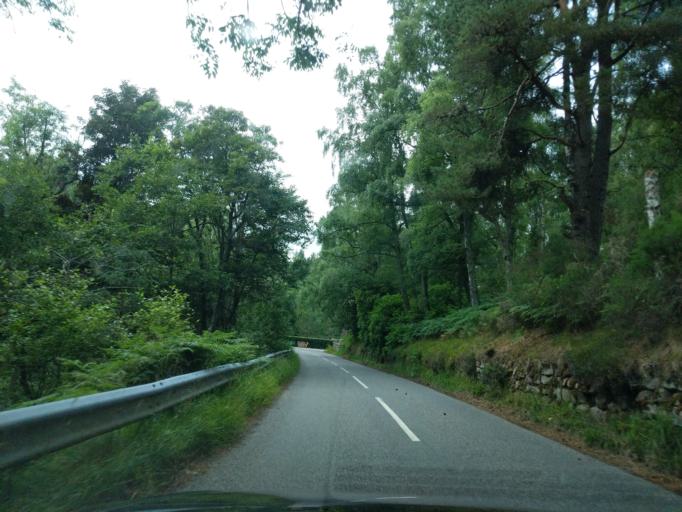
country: GB
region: Scotland
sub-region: Aberdeenshire
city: Aboyne
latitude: 57.0640
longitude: -2.8179
